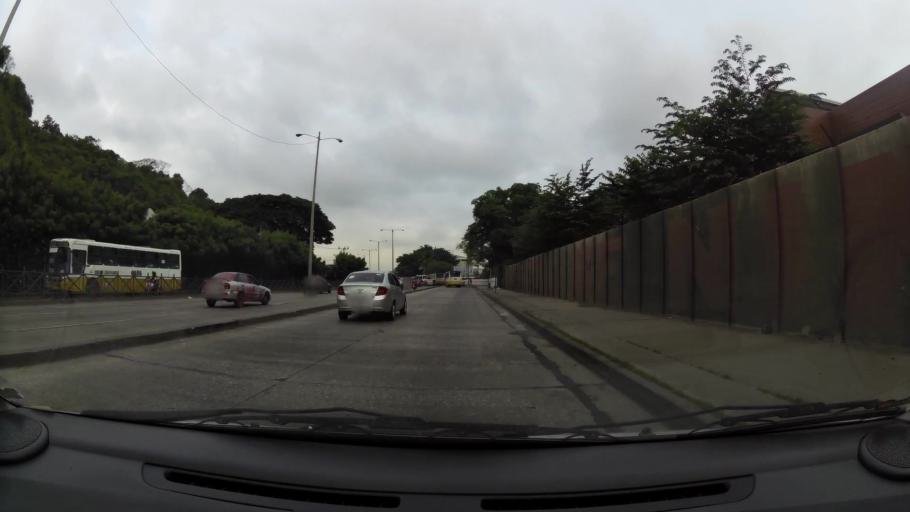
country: EC
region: Guayas
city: Eloy Alfaro
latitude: -2.1787
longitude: -79.8845
